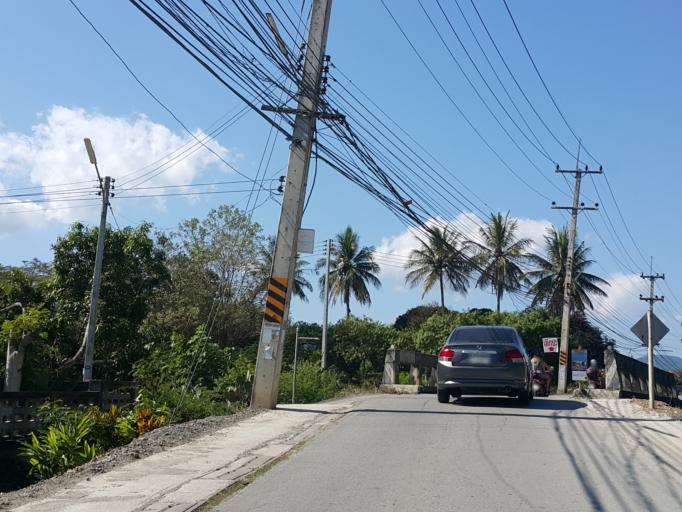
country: TH
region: Chiang Mai
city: San Sai
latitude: 18.9344
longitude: 98.9357
